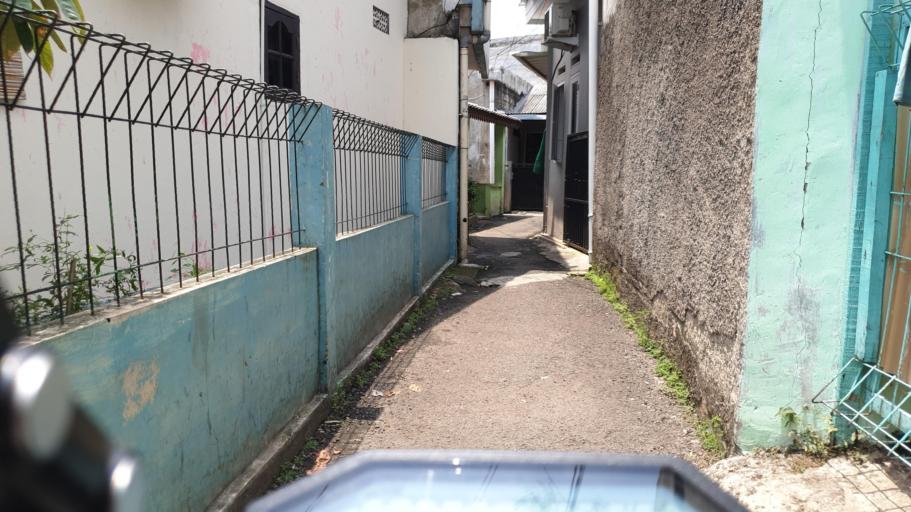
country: ID
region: West Java
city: Depok
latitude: -6.3326
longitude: 106.8296
